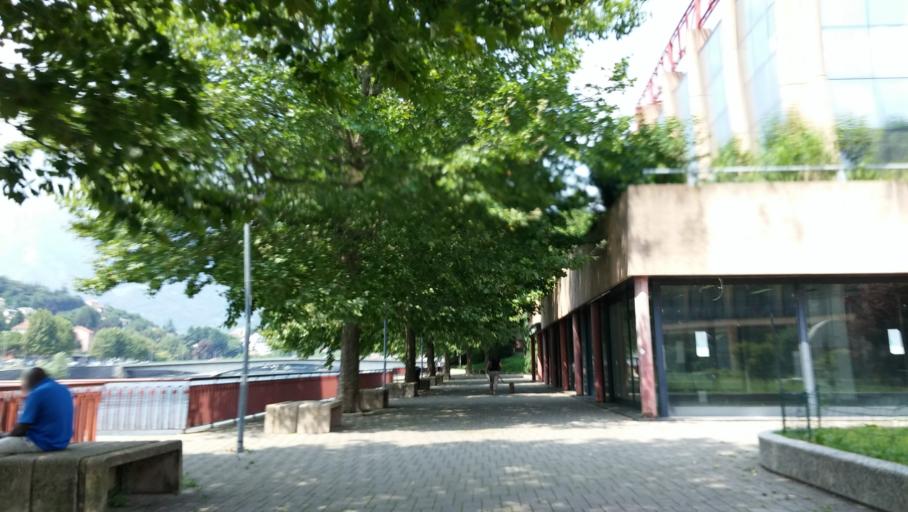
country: IT
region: Lombardy
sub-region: Provincia di Lecco
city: Lecco
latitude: 45.8483
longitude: 9.3926
